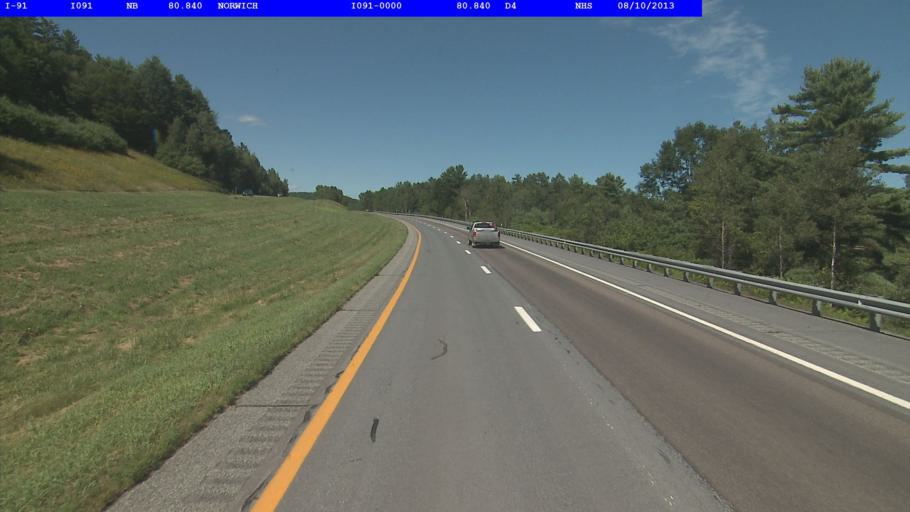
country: US
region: New Hampshire
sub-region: Grafton County
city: Lyme
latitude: 43.7660
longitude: -72.2239
